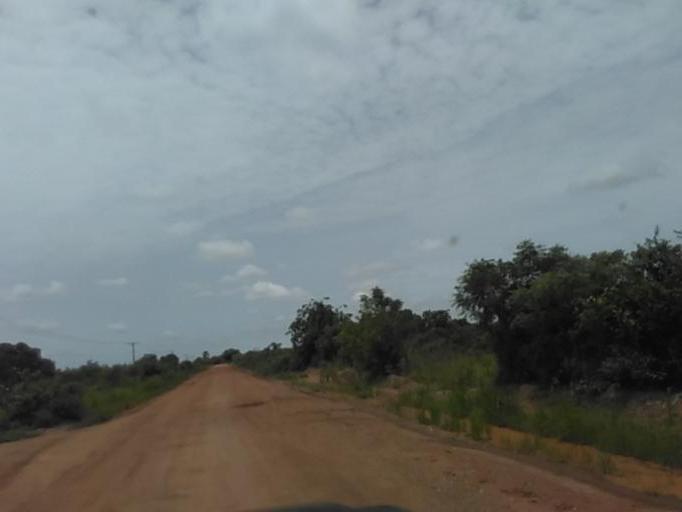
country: GH
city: Akropong
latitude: 6.0695
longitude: 0.2845
